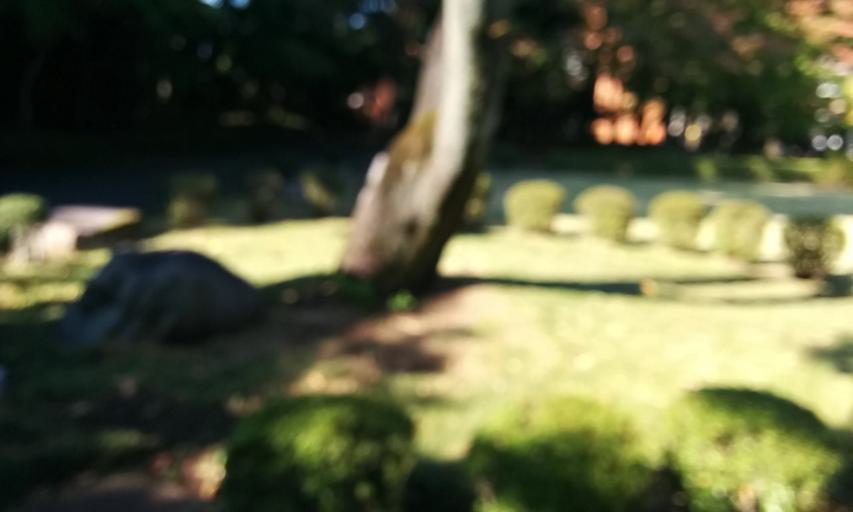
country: JP
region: Tokyo
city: Mitaka-shi
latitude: 35.6685
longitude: 139.5813
